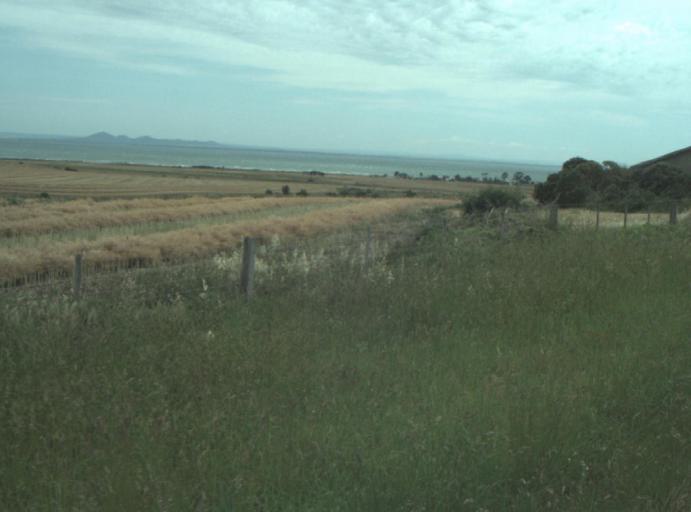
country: AU
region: Victoria
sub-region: Greater Geelong
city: Clifton Springs
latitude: -38.1258
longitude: 144.6268
